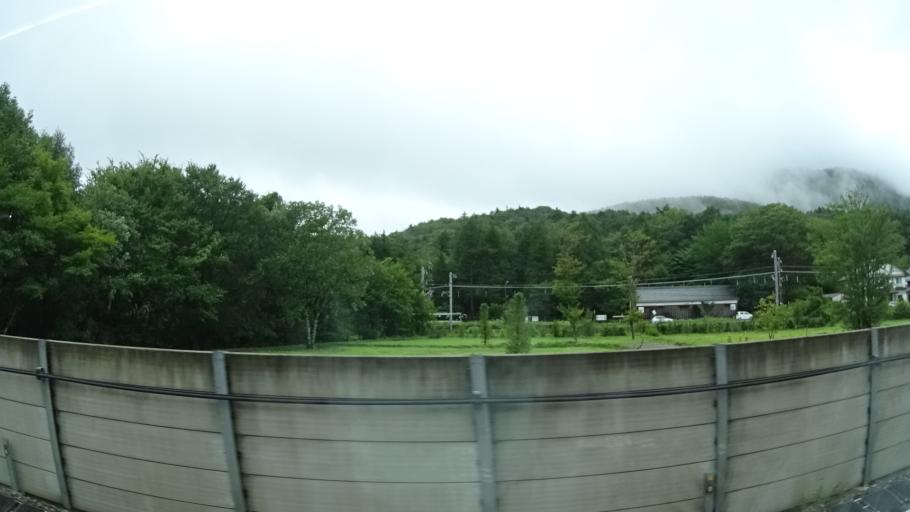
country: JP
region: Nagano
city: Komoro
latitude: 36.3427
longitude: 138.6021
